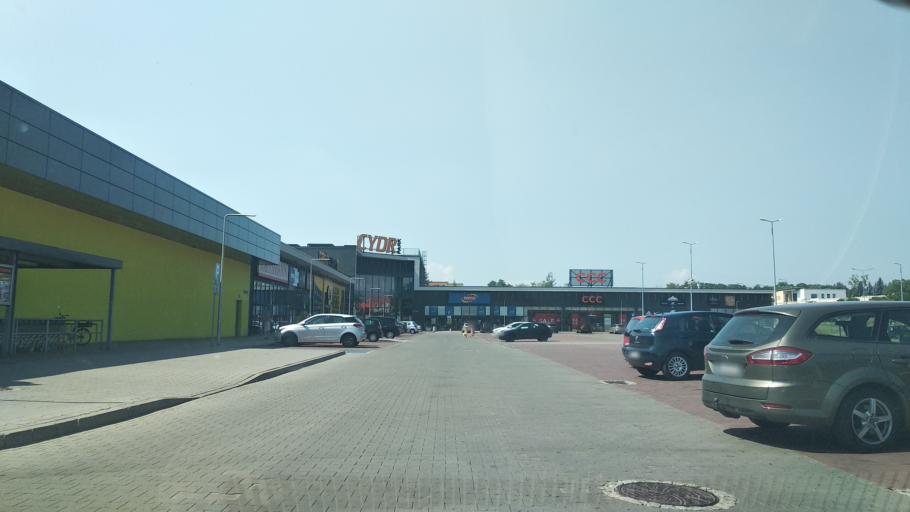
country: PL
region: Silesian Voivodeship
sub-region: Powiat tarnogorski
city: Radzionkow
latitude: 50.3957
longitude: 18.8963
